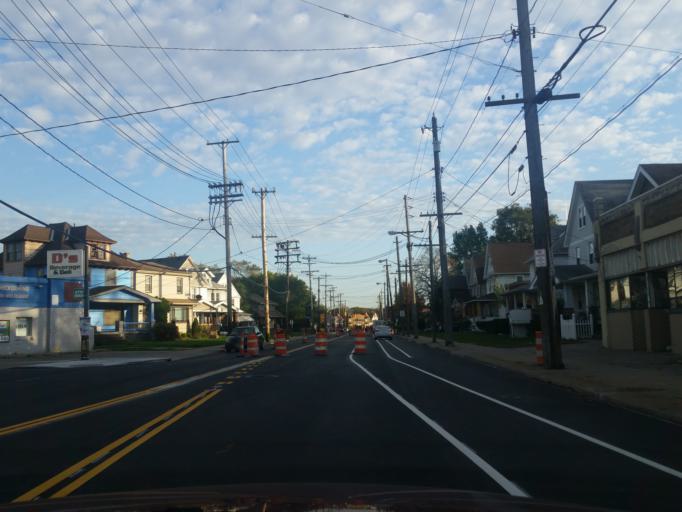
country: US
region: Ohio
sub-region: Cuyahoga County
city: Brooklyn Heights
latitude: 41.4377
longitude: -81.6991
